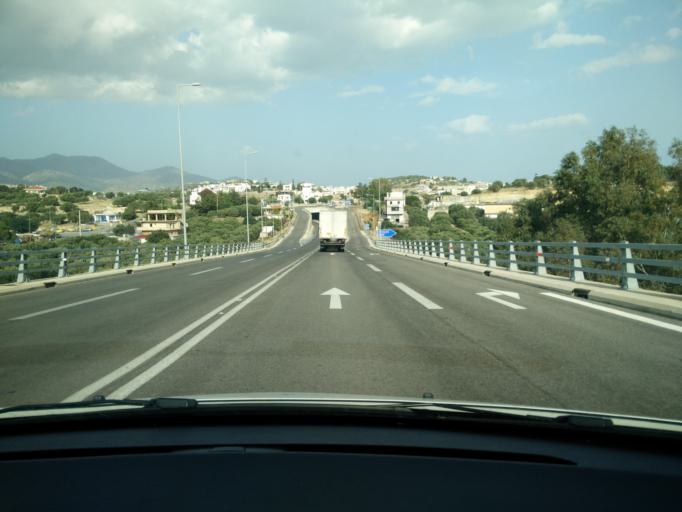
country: GR
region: Crete
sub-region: Nomos Lasithiou
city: Agios Nikolaos
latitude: 35.1819
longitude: 25.7033
